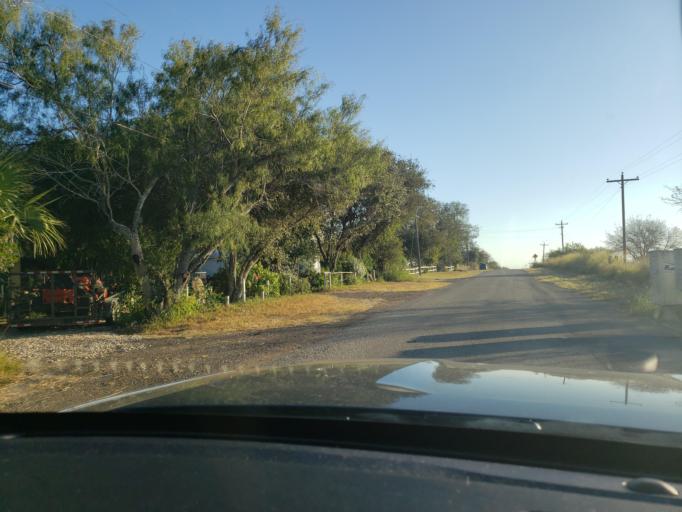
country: US
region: Texas
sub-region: Bee County
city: Beeville
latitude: 28.4170
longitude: -97.7199
